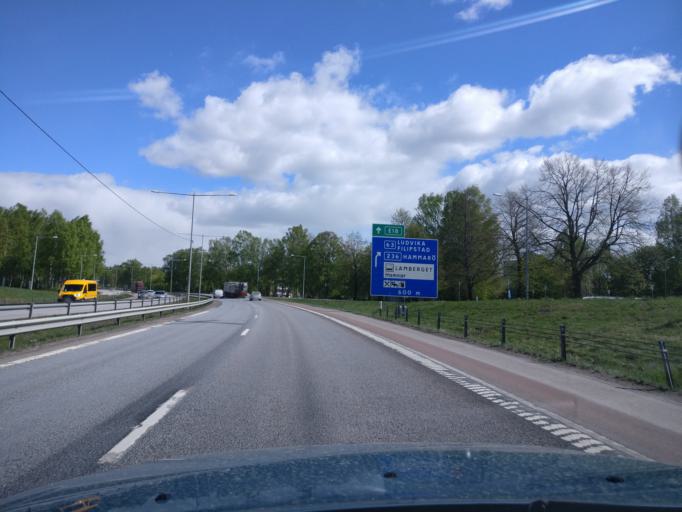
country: SE
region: Vaermland
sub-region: Karlstads Kommun
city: Karlstad
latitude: 59.3955
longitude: 13.5183
